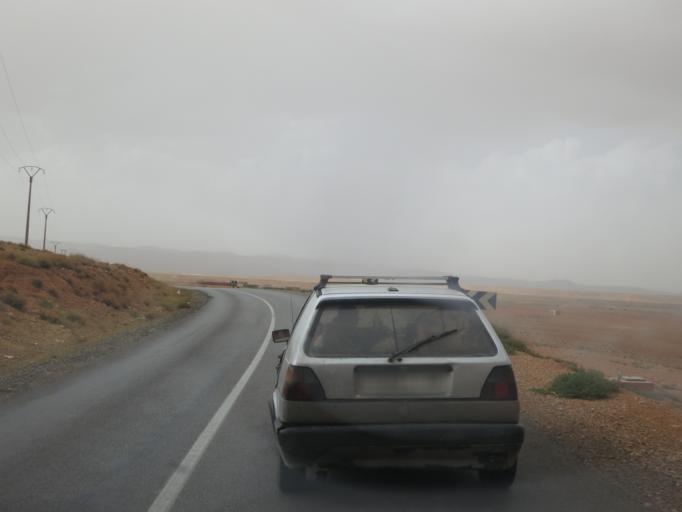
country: MA
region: Meknes-Tafilalet
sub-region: Khenifra
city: Itzer
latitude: 32.8702
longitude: -4.9438
